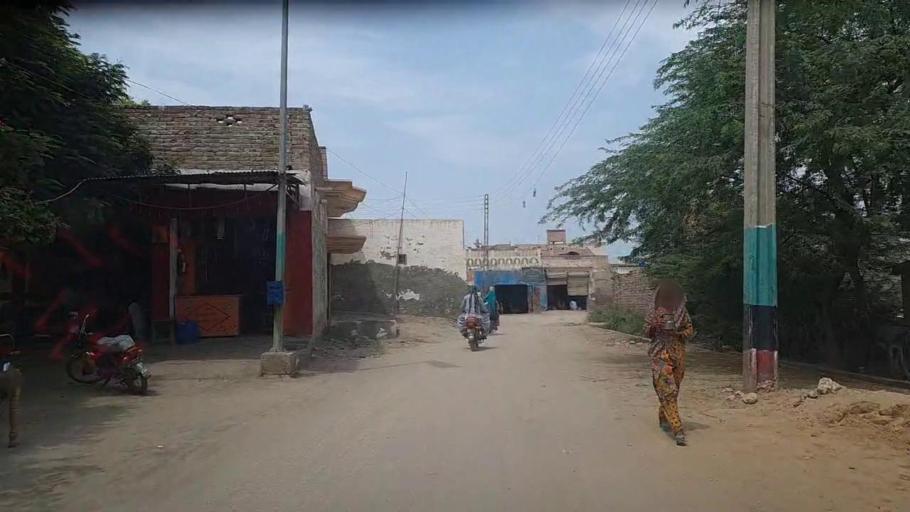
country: PK
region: Sindh
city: Bhiria
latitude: 26.8919
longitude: 68.2841
